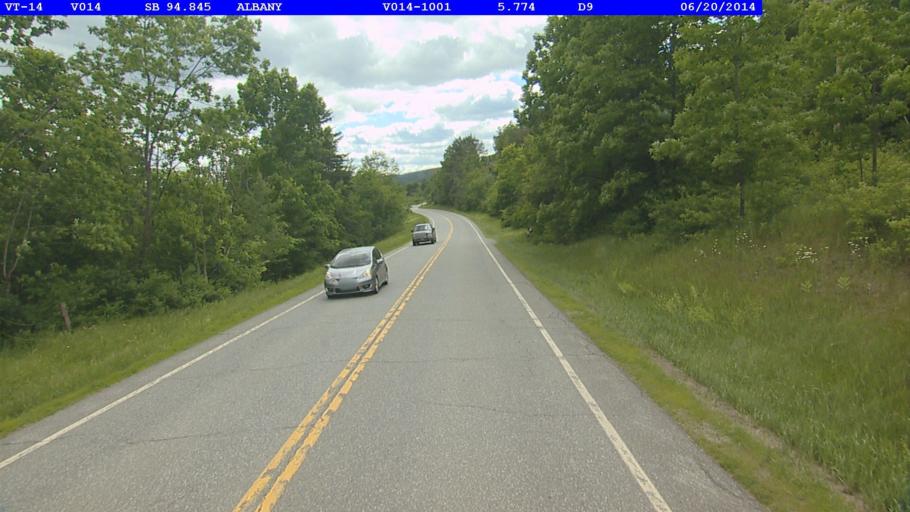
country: US
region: Vermont
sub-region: Orleans County
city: Newport
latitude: 44.7695
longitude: -72.3331
